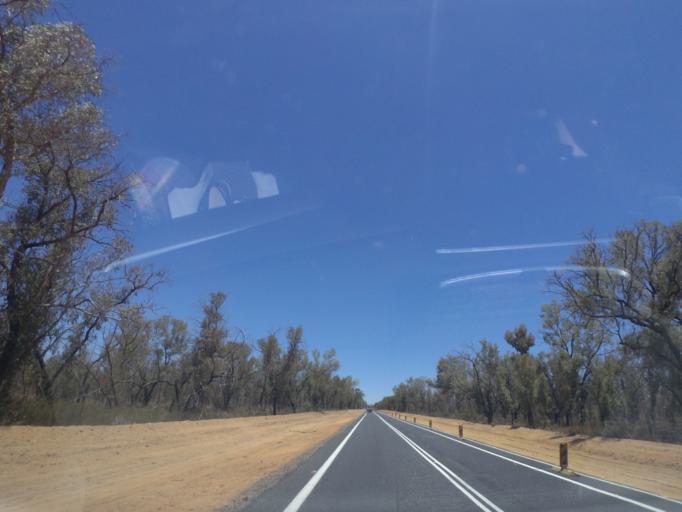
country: AU
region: New South Wales
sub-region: Warrumbungle Shire
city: Coonabarabran
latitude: -30.9332
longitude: 149.4276
